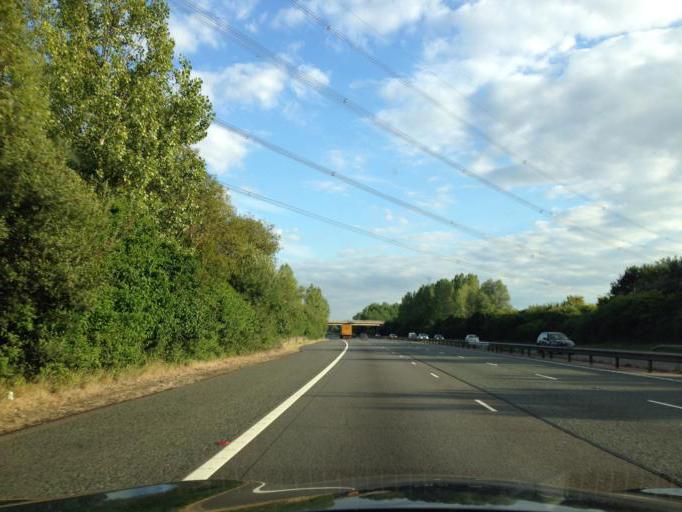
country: GB
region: England
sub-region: Oxfordshire
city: Wheatley
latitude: 51.7567
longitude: -1.1058
